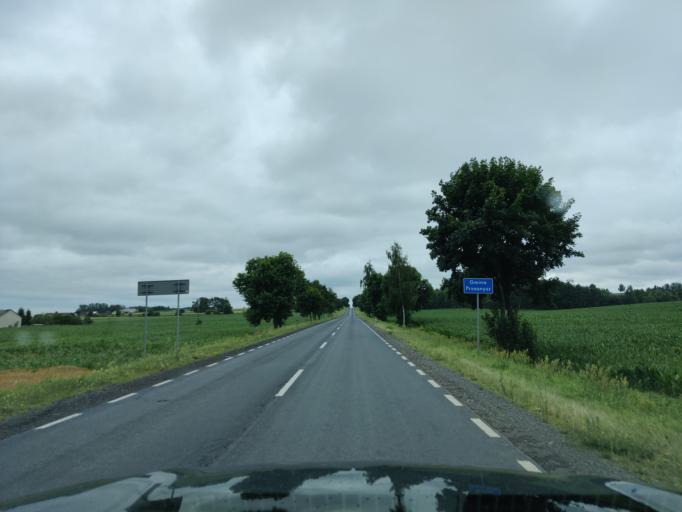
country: PL
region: Masovian Voivodeship
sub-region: Powiat przasnyski
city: Przasnysz
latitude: 53.0924
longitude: 20.8546
